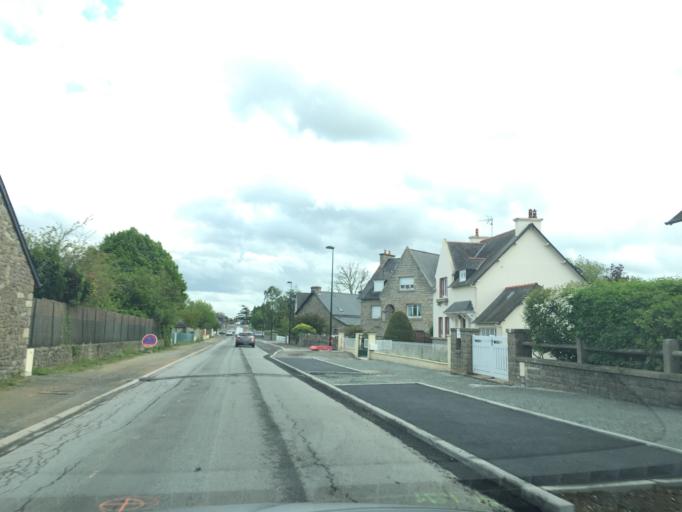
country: FR
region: Brittany
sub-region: Departement des Cotes-d'Armor
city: Ploubalay
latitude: 48.5844
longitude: -2.1430
